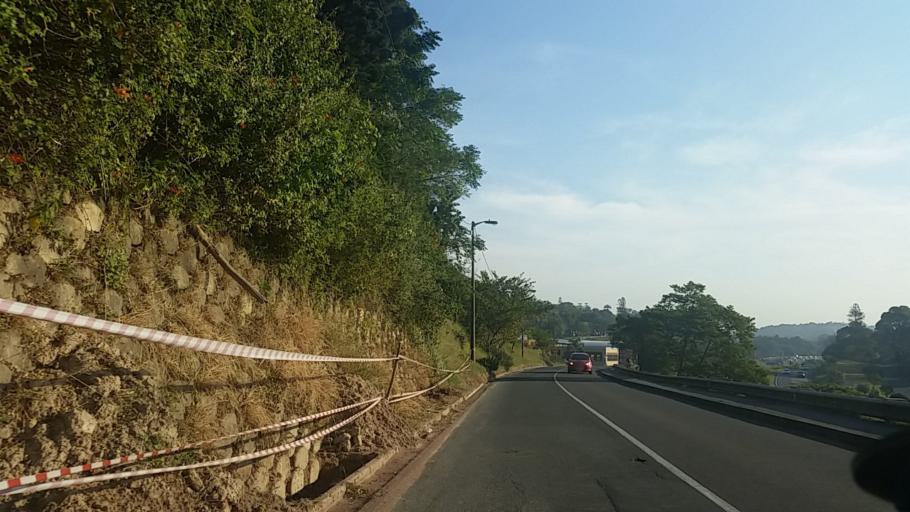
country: ZA
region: KwaZulu-Natal
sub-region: eThekwini Metropolitan Municipality
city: Berea
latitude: -29.8355
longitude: 30.9102
